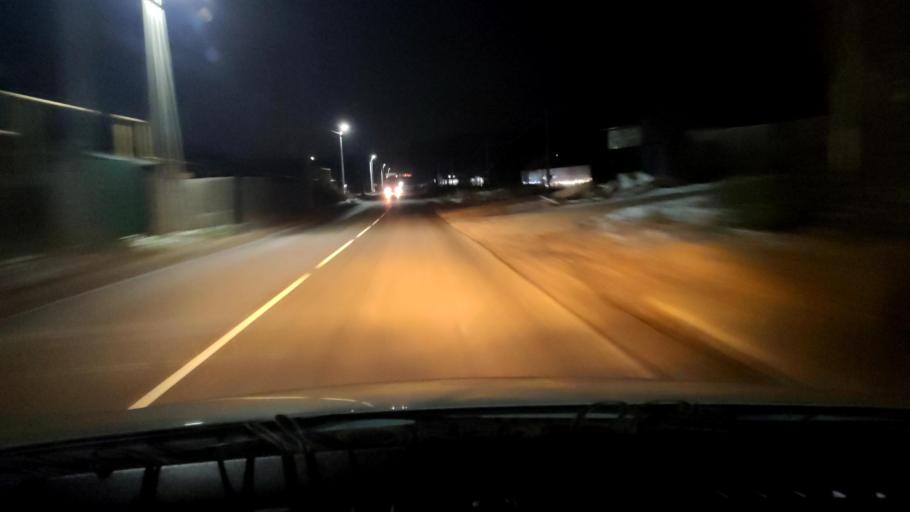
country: RU
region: Voronezj
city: Podgornoye
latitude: 51.8174
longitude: 39.0749
